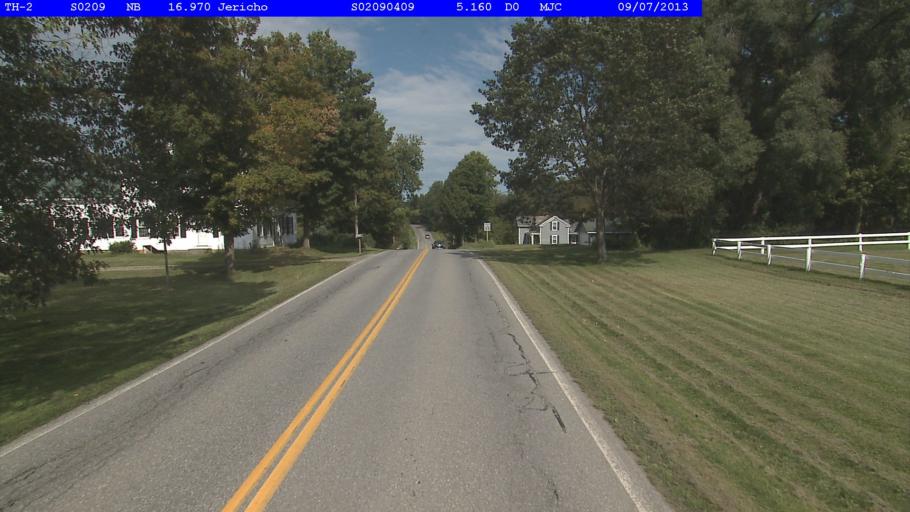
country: US
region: Vermont
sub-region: Chittenden County
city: Jericho
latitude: 44.4954
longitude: -72.9876
